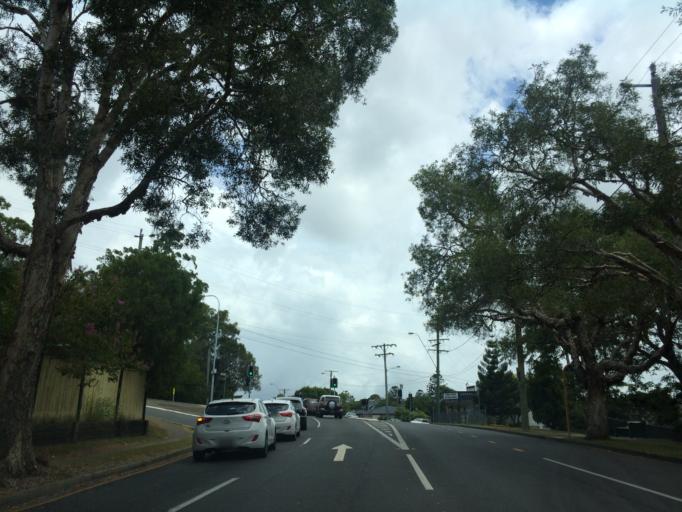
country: AU
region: Queensland
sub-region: Brisbane
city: Morningside
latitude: -27.4692
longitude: 153.0638
